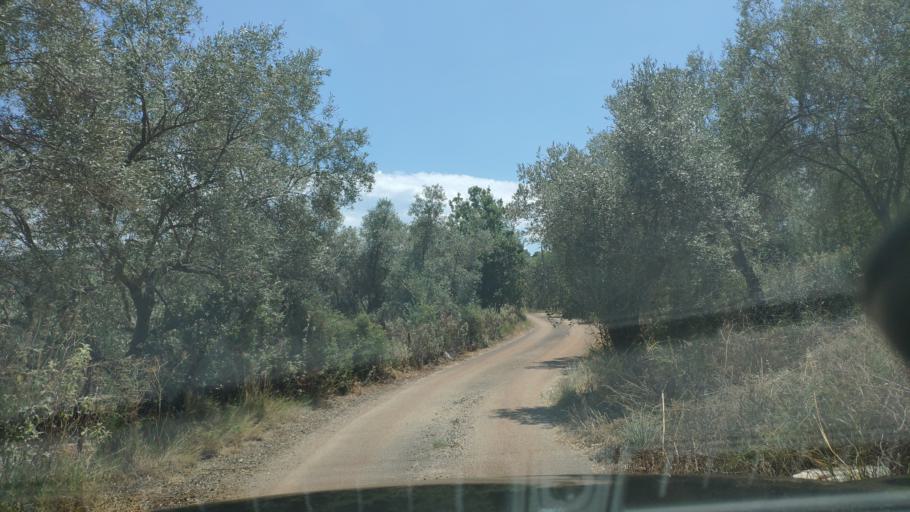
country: GR
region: West Greece
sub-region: Nomos Aitolias kai Akarnanias
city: Amfilochia
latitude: 38.9076
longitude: 21.1068
